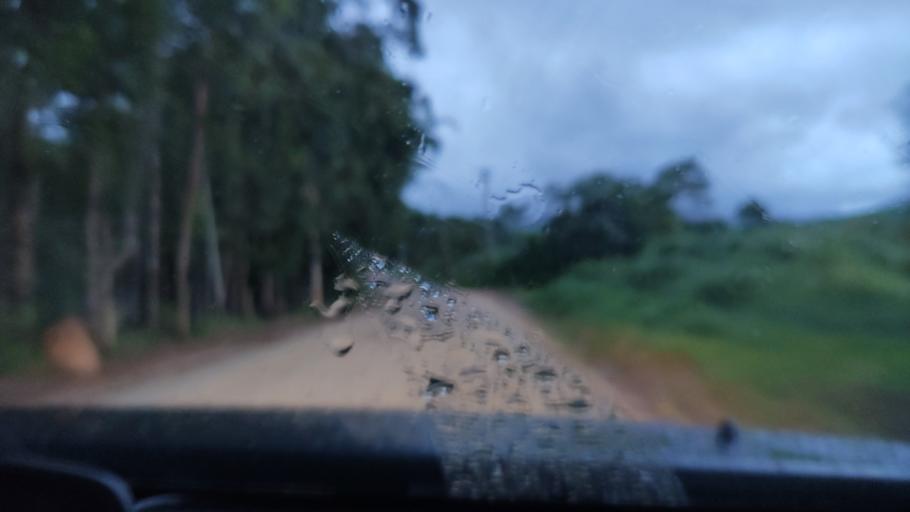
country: BR
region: Sao Paulo
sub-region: Serra Negra
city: Serra Negra
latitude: -22.5978
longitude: -46.6278
